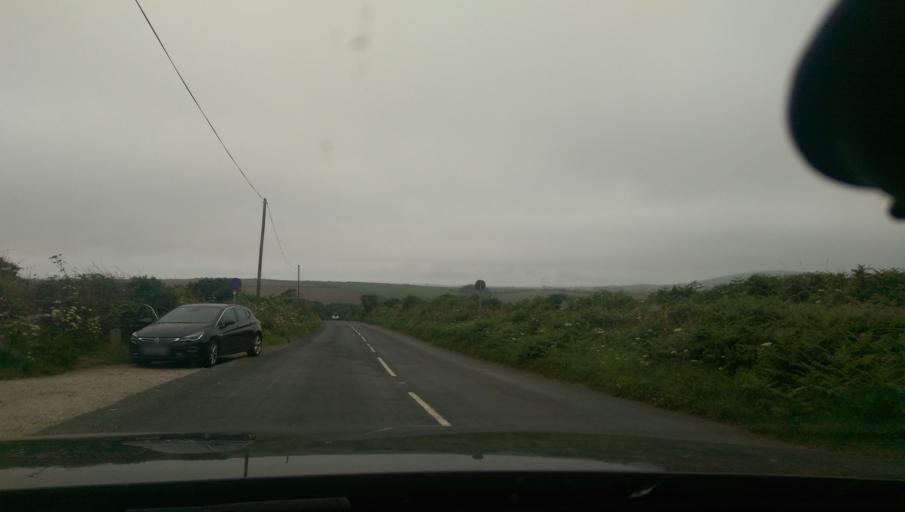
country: GB
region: England
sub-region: Cornwall
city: St. Buryan
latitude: 50.0929
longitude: -5.6226
